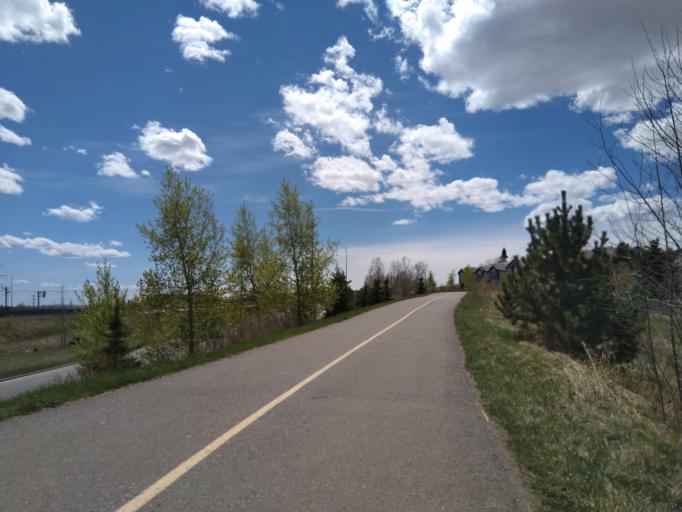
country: CA
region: Alberta
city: Calgary
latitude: 51.0416
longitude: -114.1658
